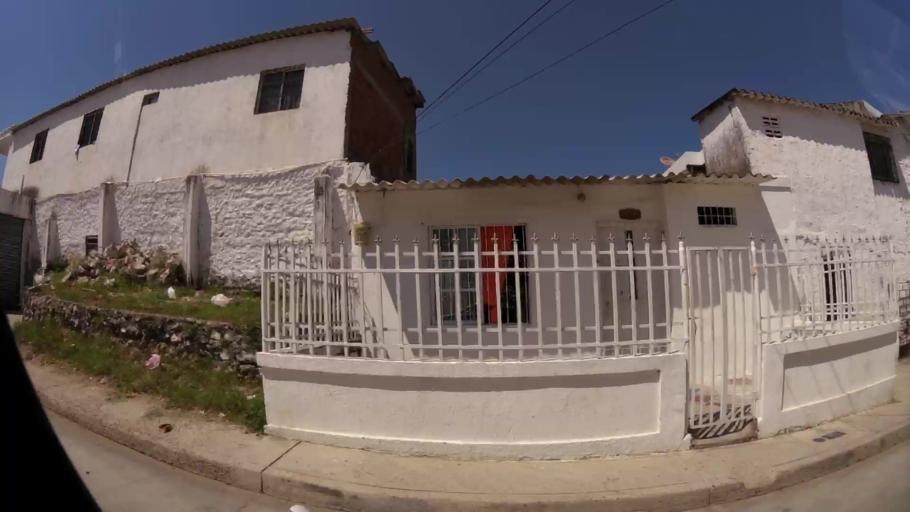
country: CO
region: Bolivar
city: Cartagena
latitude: 10.4329
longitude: -75.5295
